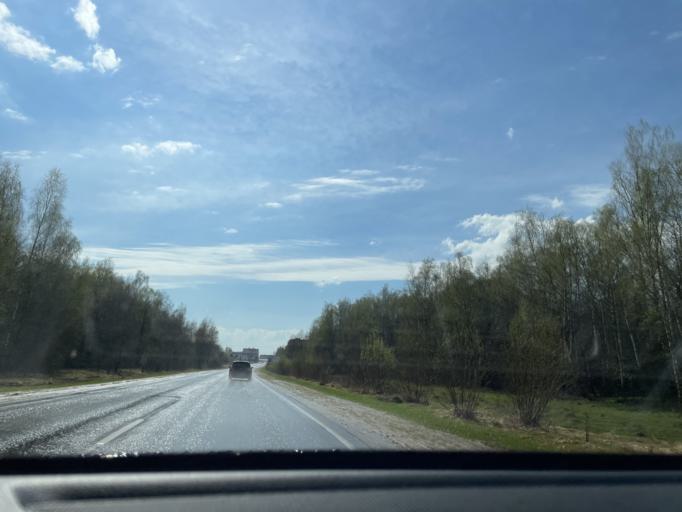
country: RU
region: Tula
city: Aleksin
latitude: 54.5128
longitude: 37.1328
